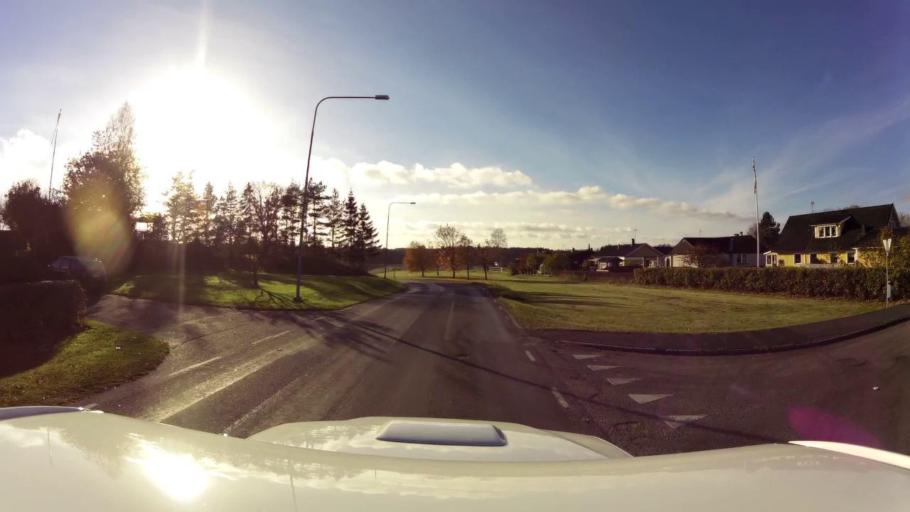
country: SE
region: OEstergoetland
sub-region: Linkopings Kommun
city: Vikingstad
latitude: 58.2868
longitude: 15.4448
